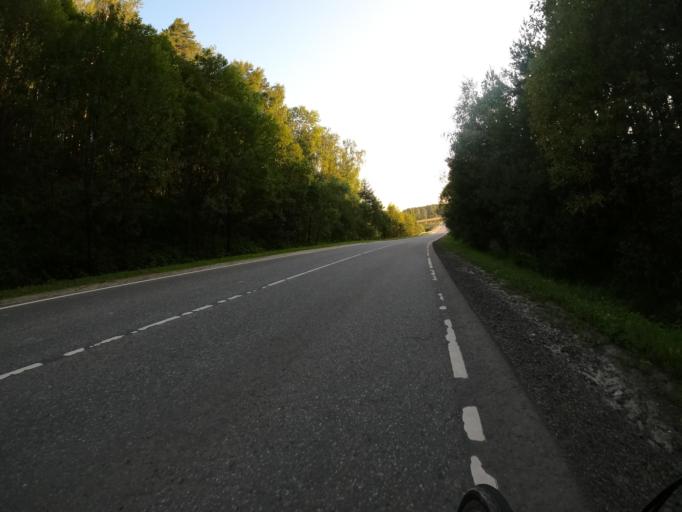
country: RU
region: Moskovskaya
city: Meshcherino
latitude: 55.1077
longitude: 38.3032
